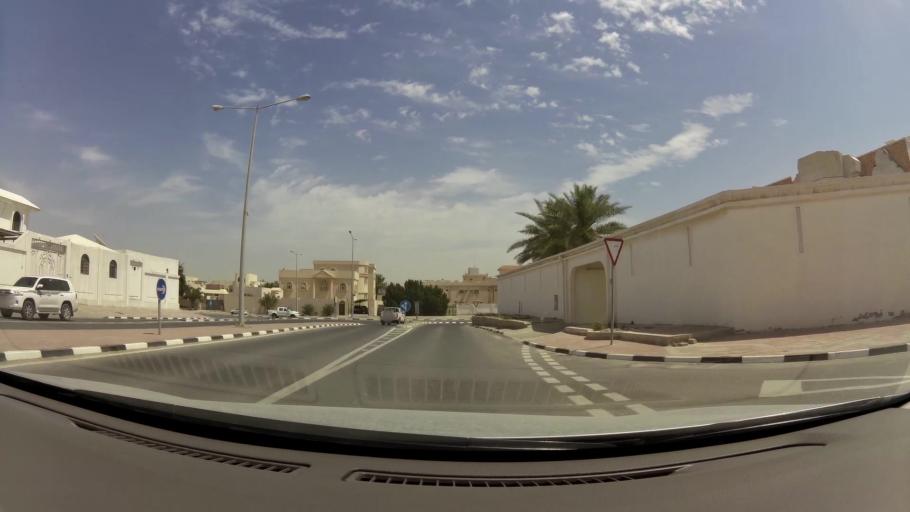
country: QA
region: Baladiyat ar Rayyan
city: Ar Rayyan
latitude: 25.2837
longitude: 51.4197
